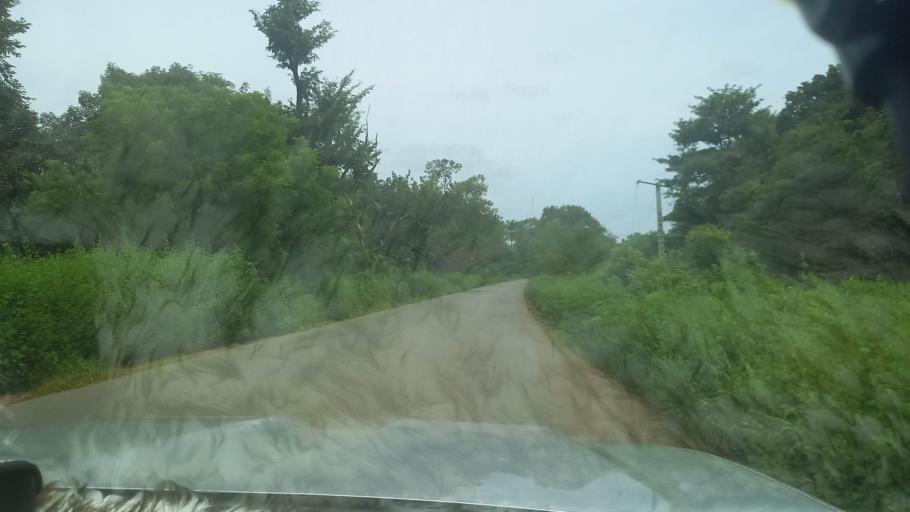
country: SN
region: Kolda
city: Marsassoum
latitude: 12.9554
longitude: -16.0053
